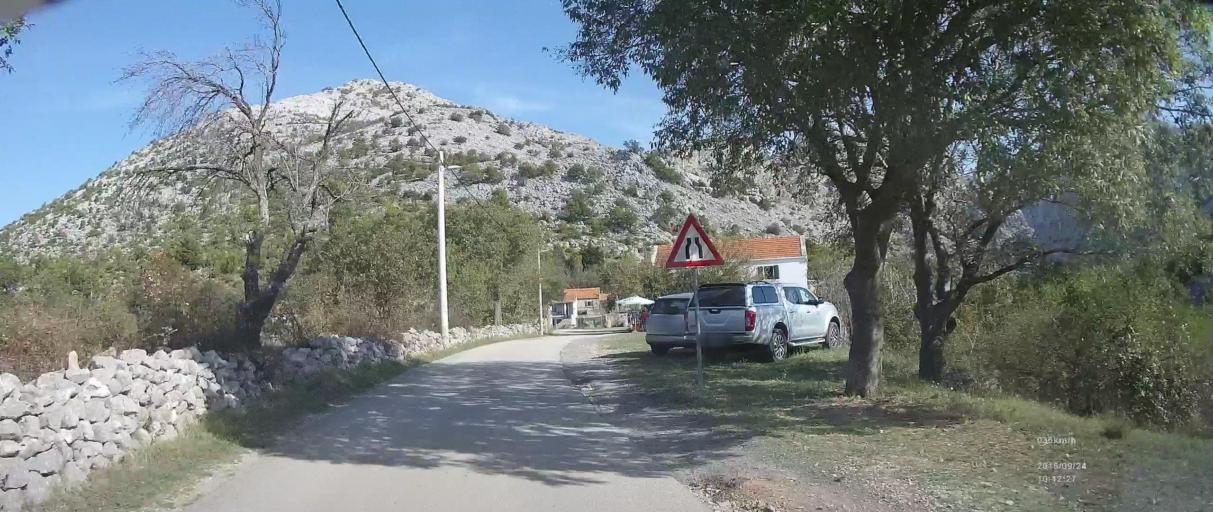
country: HR
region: Zadarska
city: Starigrad
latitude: 44.2914
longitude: 15.4549
